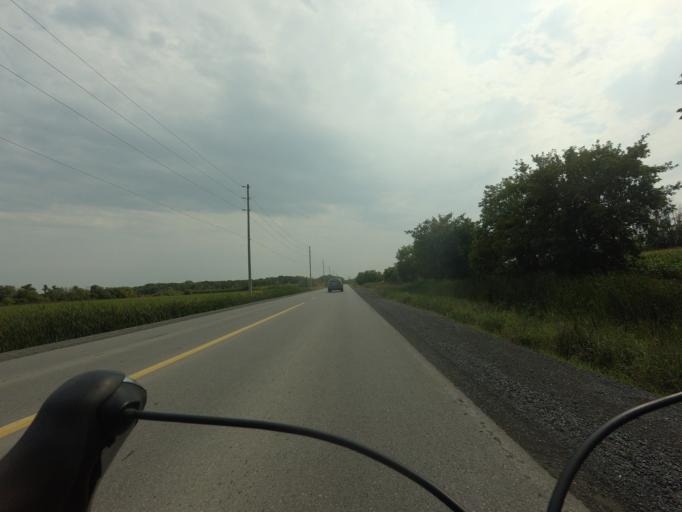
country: CA
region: Ontario
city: Bells Corners
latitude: 45.2505
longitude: -75.7638
